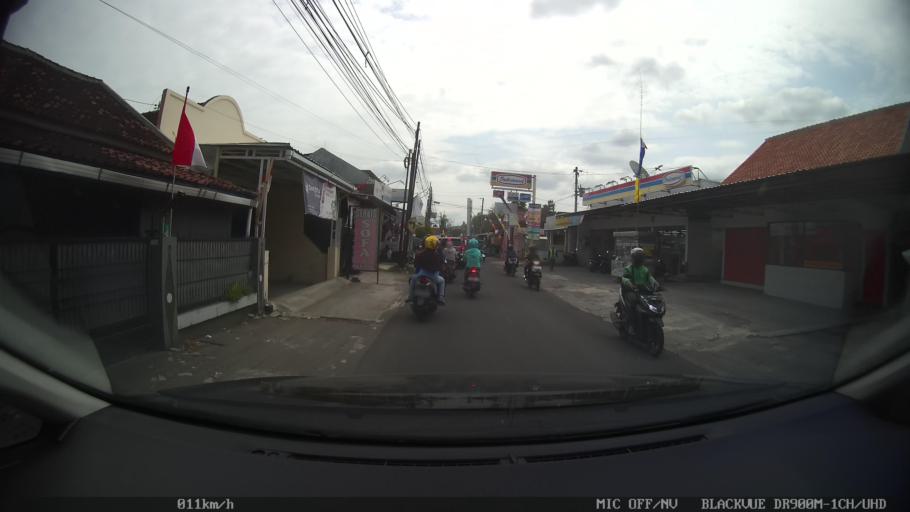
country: ID
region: Daerah Istimewa Yogyakarta
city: Depok
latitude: -7.7528
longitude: 110.4422
